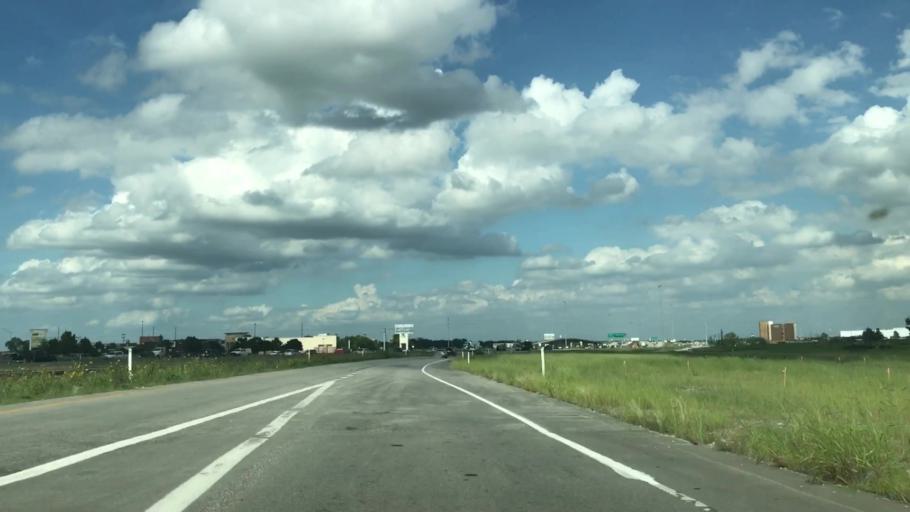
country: US
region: Texas
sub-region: Dallas County
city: Coppell
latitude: 32.9639
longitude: -97.0363
